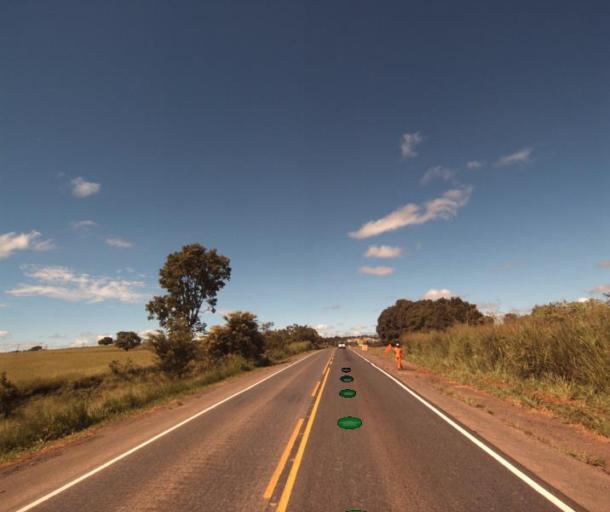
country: BR
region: Goias
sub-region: Rialma
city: Rialma
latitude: -15.2957
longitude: -49.5691
